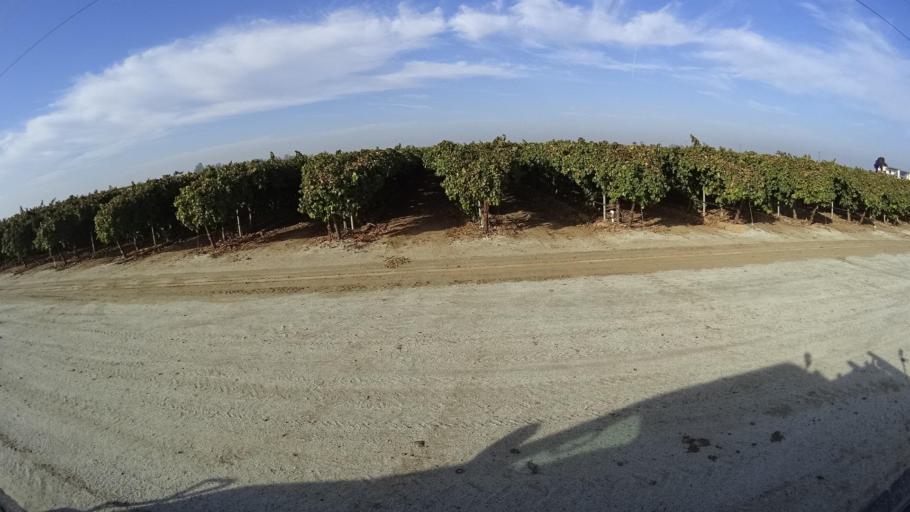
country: US
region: California
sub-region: Kern County
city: McFarland
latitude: 35.6800
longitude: -119.2049
